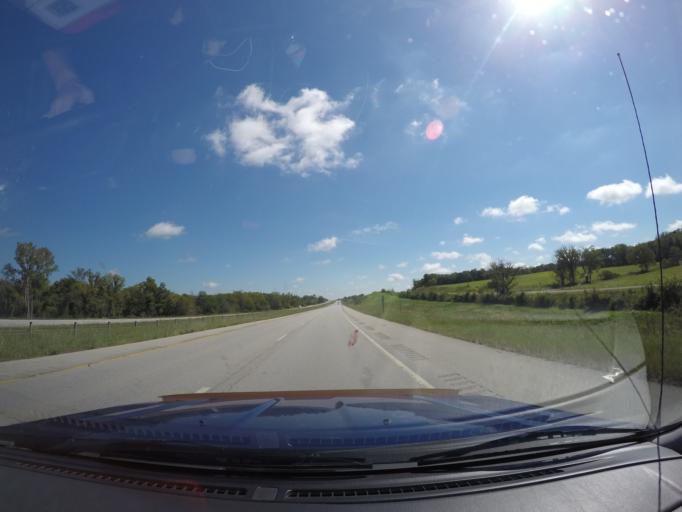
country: US
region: Kansas
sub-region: Douglas County
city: Eudora
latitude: 38.9431
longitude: -95.0659
